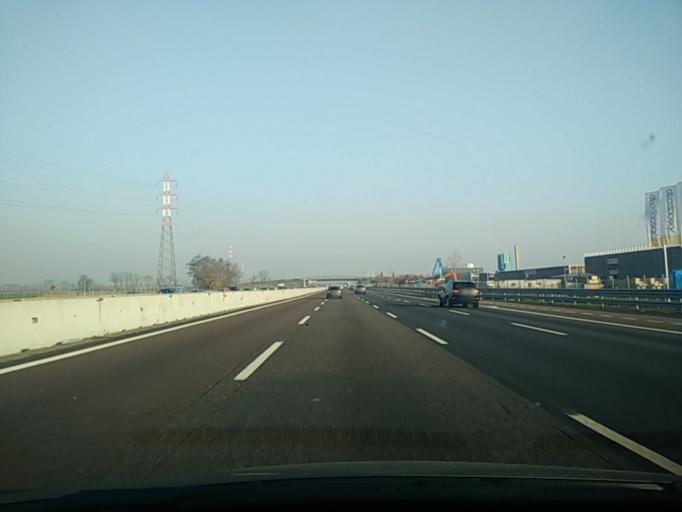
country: IT
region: Lombardy
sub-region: Citta metropolitana di Milano
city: Basiano
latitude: 45.5899
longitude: 9.4739
